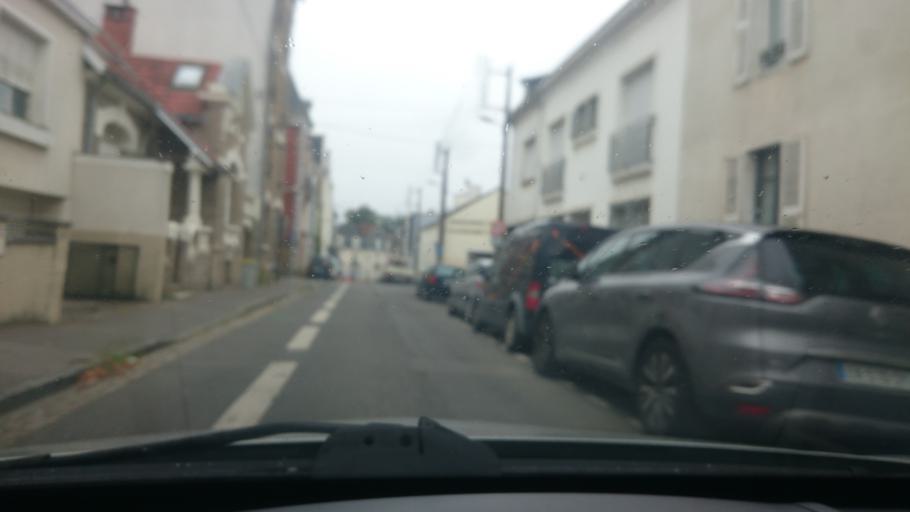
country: FR
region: Pays de la Loire
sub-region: Departement de la Loire-Atlantique
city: Nantes
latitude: 47.2176
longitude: -1.5769
